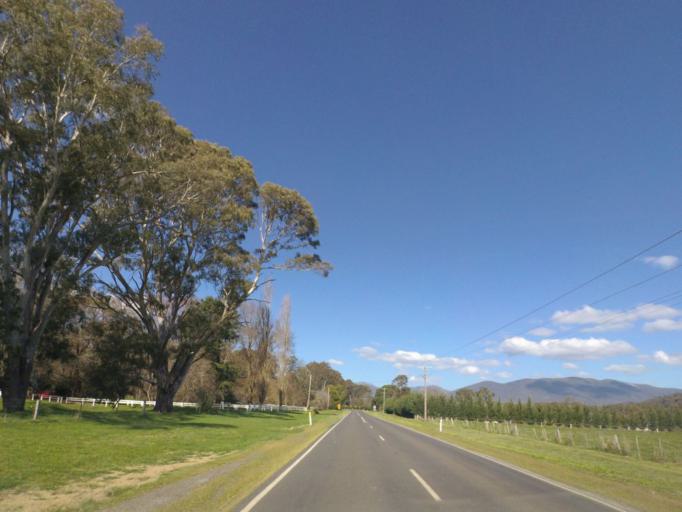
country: AU
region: Victoria
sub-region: Murrindindi
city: Alexandra
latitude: -37.2442
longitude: 145.7725
